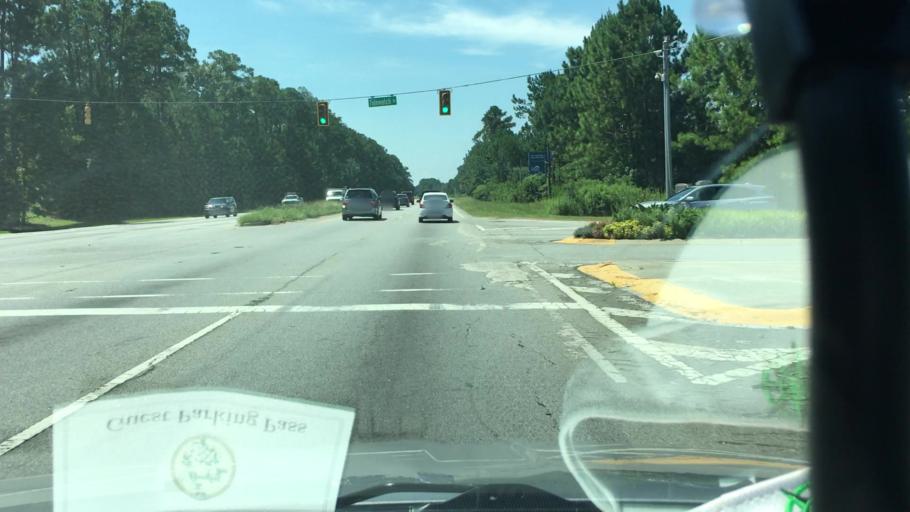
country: US
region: South Carolina
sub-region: Beaufort County
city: Bluffton
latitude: 32.3117
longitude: -80.9349
